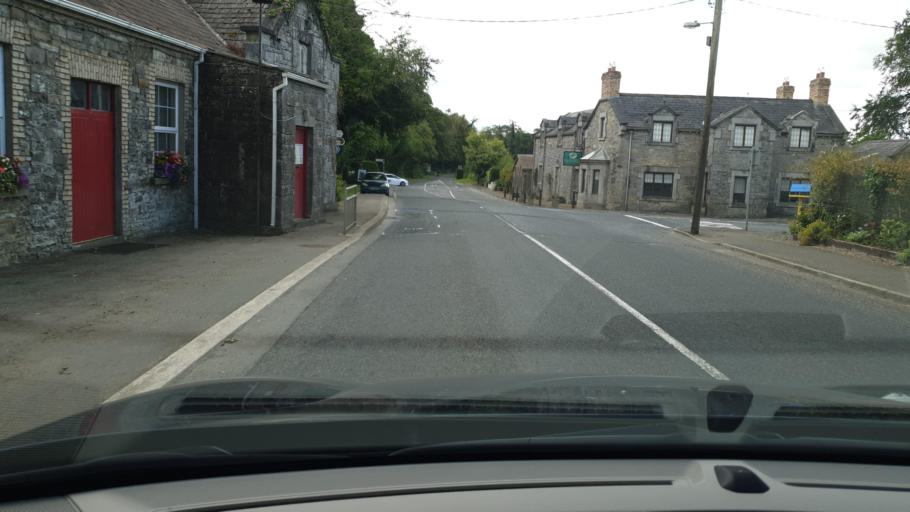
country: IE
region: Leinster
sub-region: An Mhi
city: Dunshaughlin
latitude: 53.5422
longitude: -6.6206
